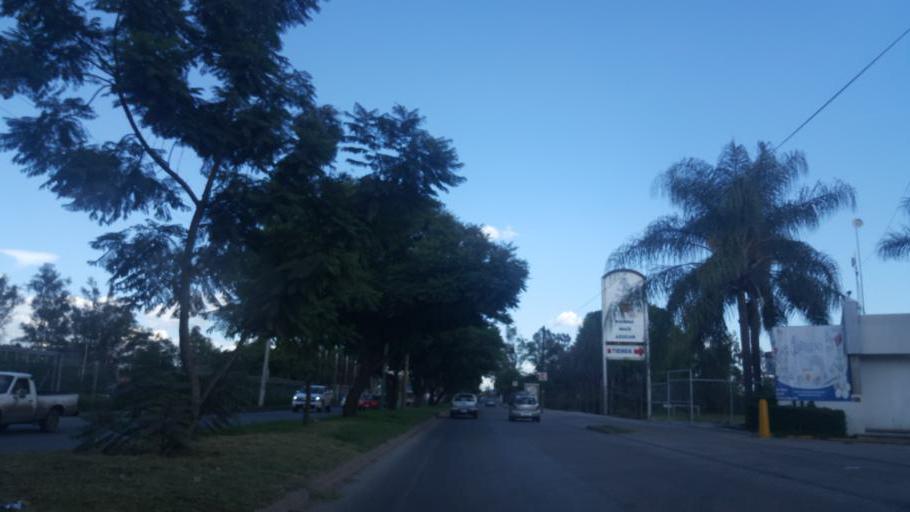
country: MX
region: Guanajuato
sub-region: Leon
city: San Jose de Duran (Los Troncoso)
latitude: 21.0947
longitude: -101.6928
